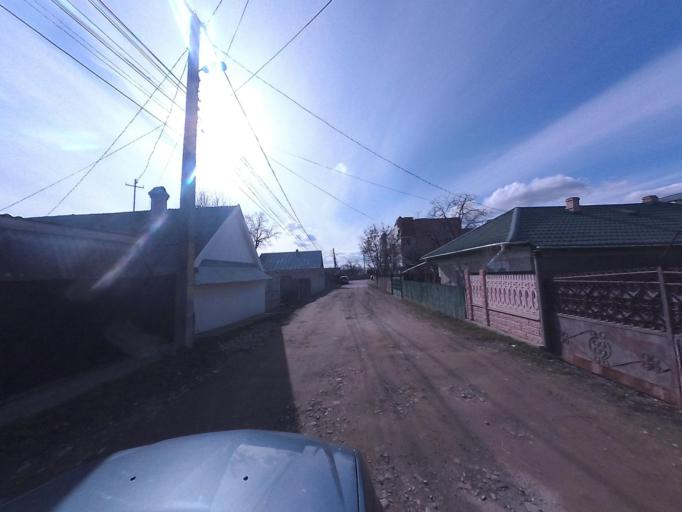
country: RO
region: Neamt
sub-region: Oras Targu Neamt
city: Targu Neamt
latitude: 47.2024
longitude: 26.3597
